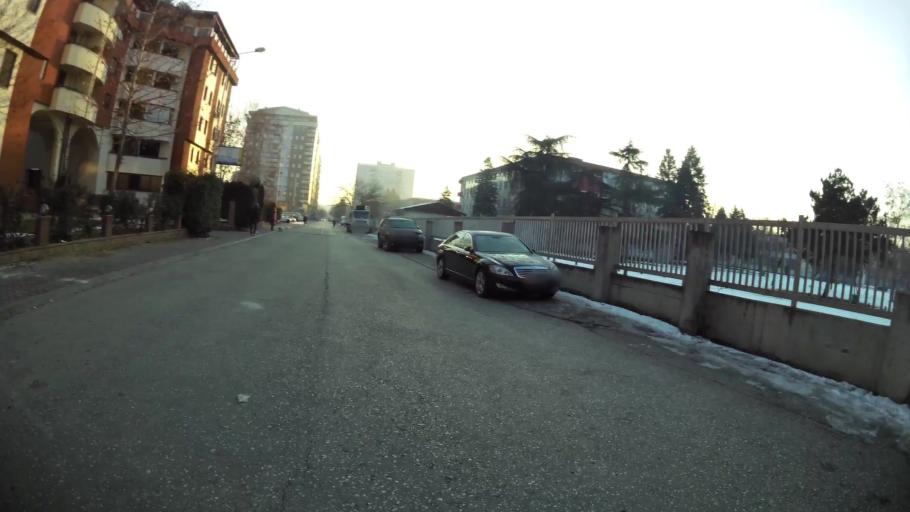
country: MK
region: Karpos
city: Skopje
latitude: 42.0057
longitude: 21.4071
